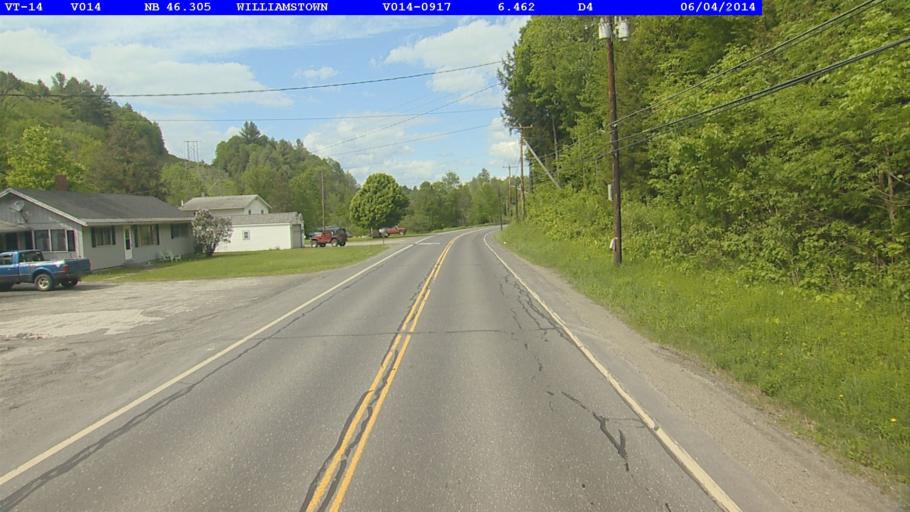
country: US
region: Vermont
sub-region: Orange County
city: Williamstown
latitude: 44.1469
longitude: -72.5235
